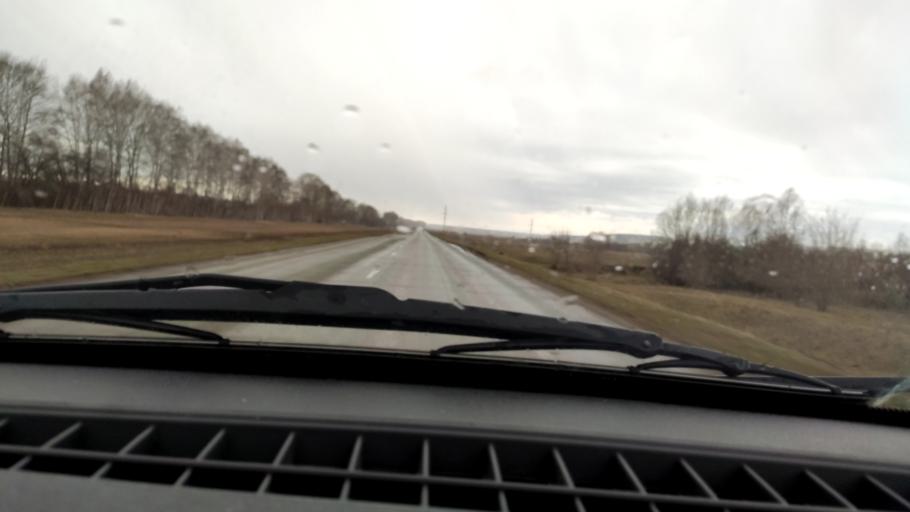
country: RU
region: Bashkortostan
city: Chekmagush
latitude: 55.1212
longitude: 54.7351
